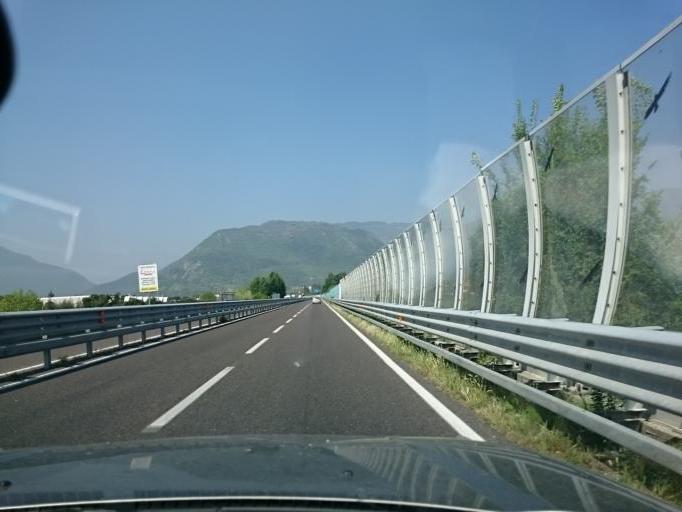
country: IT
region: Veneto
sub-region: Provincia di Vicenza
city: Romano d'Ezzelino
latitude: 45.7774
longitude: 11.7616
